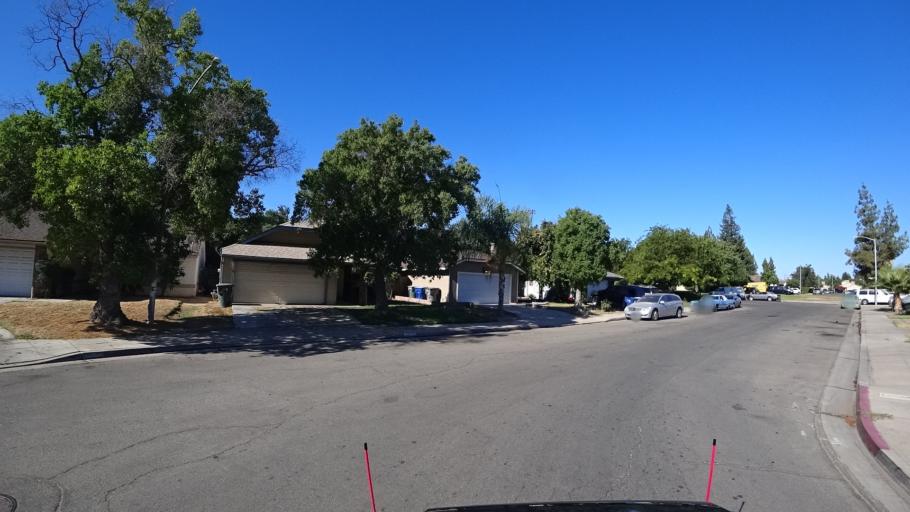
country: US
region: California
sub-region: Fresno County
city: West Park
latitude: 36.7724
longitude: -119.8573
